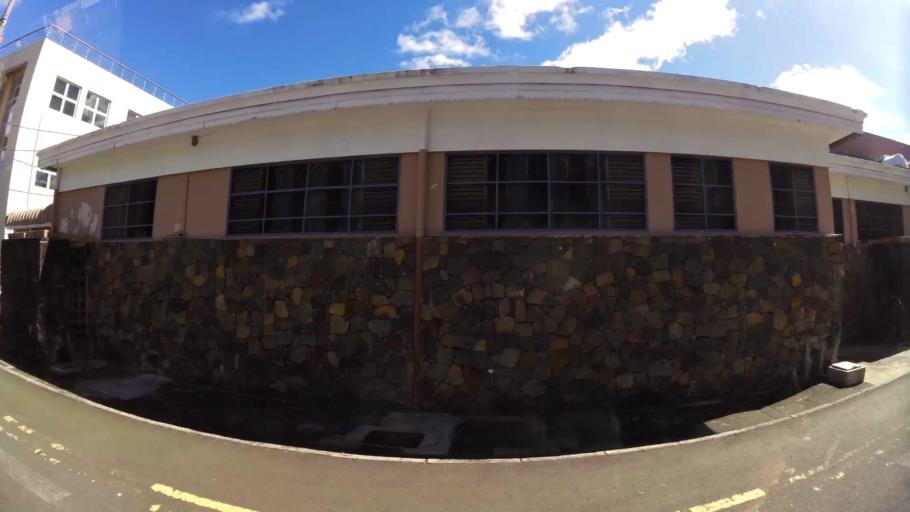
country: MU
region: Plaines Wilhems
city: Vacoas
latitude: -20.2958
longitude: 57.4933
